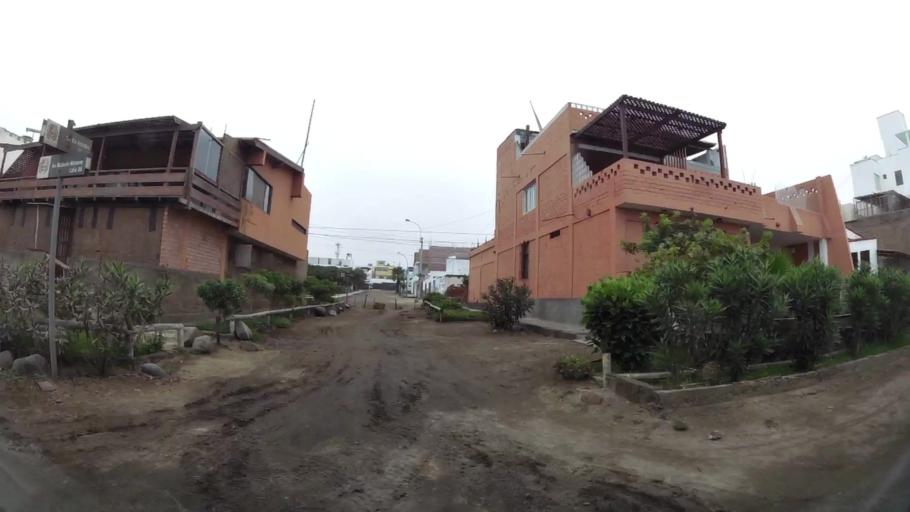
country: PE
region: Lima
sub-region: Lima
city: Punta Hermosa
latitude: -12.3379
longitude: -76.8210
